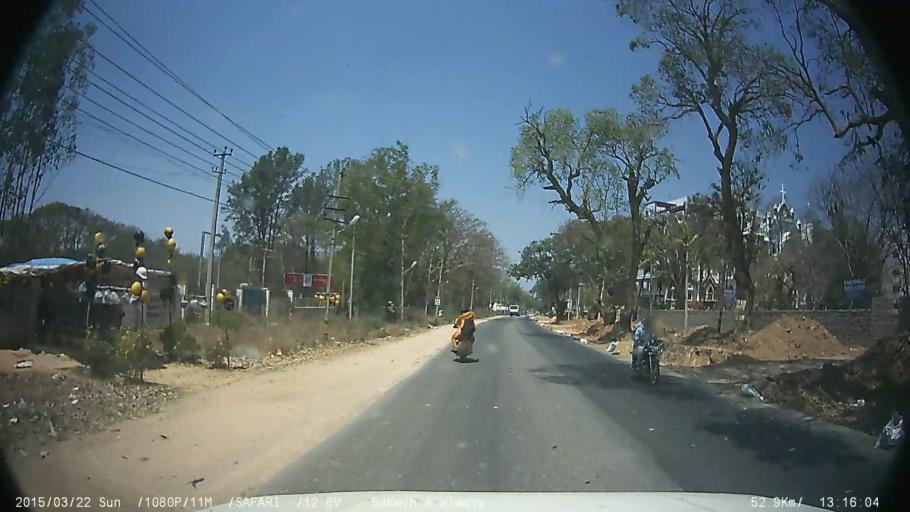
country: IN
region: Karnataka
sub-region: Bangalore Urban
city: Bangalore
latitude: 12.8277
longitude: 77.5869
